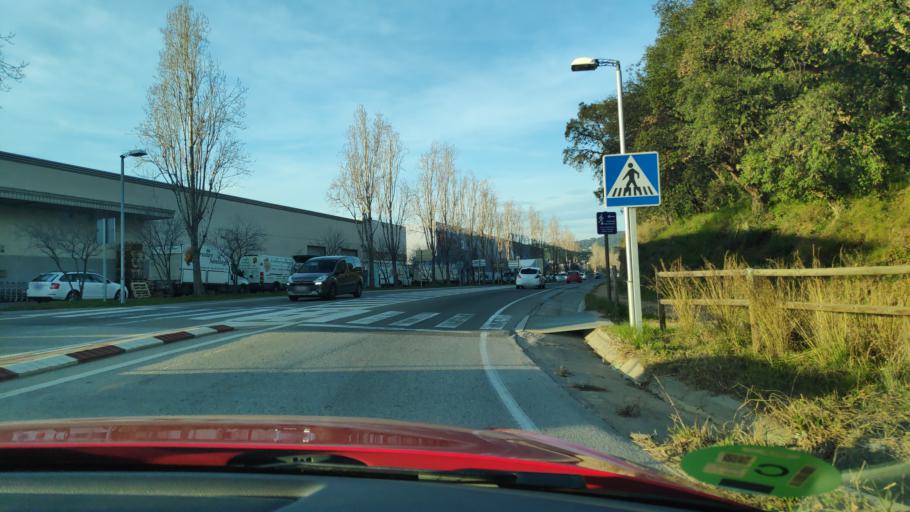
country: ES
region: Catalonia
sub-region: Provincia de Girona
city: Lloret de Mar
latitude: 41.7092
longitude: 2.8324
